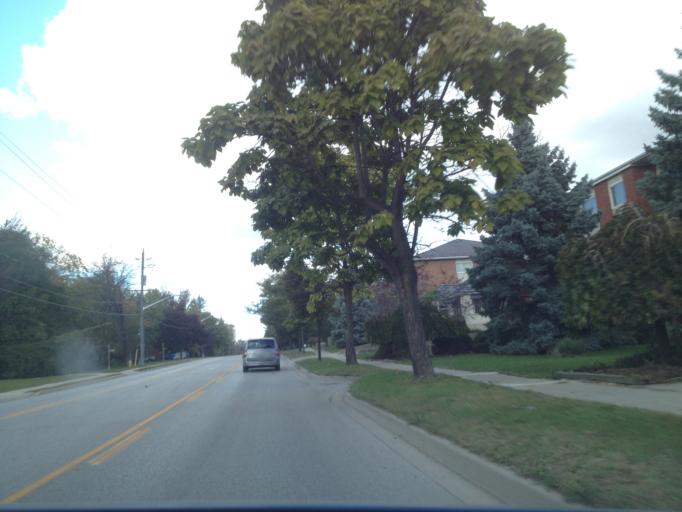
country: CA
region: Ontario
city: Amherstburg
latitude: 42.0415
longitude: -82.7393
